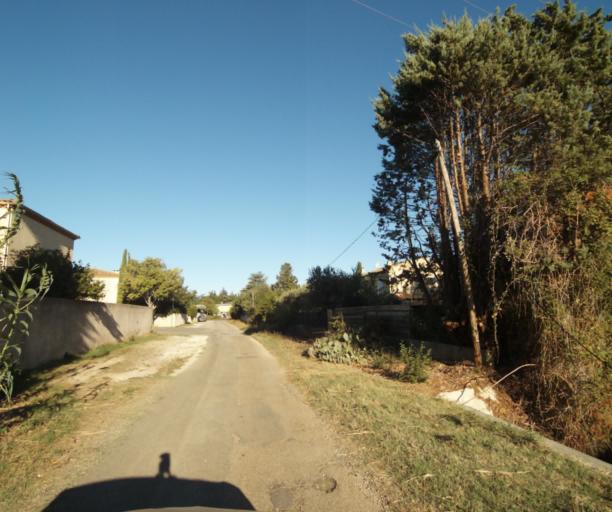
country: FR
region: Languedoc-Roussillon
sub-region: Departement du Gard
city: Bouillargues
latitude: 43.7977
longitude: 4.4386
